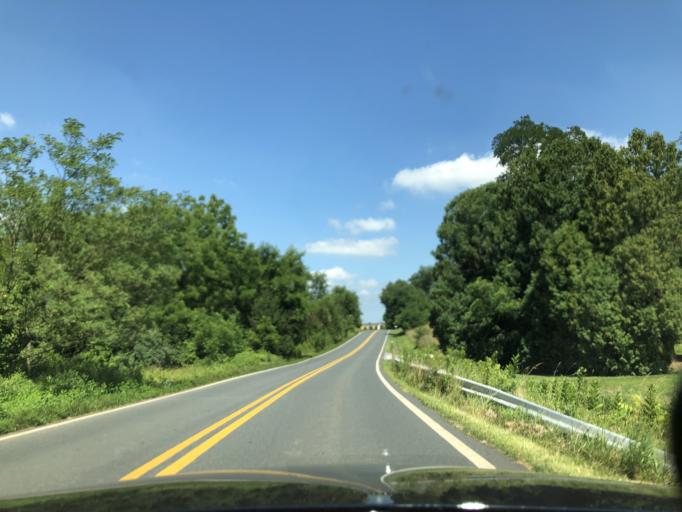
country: US
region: Maryland
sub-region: Carroll County
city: Westminster
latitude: 39.6066
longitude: -76.9774
